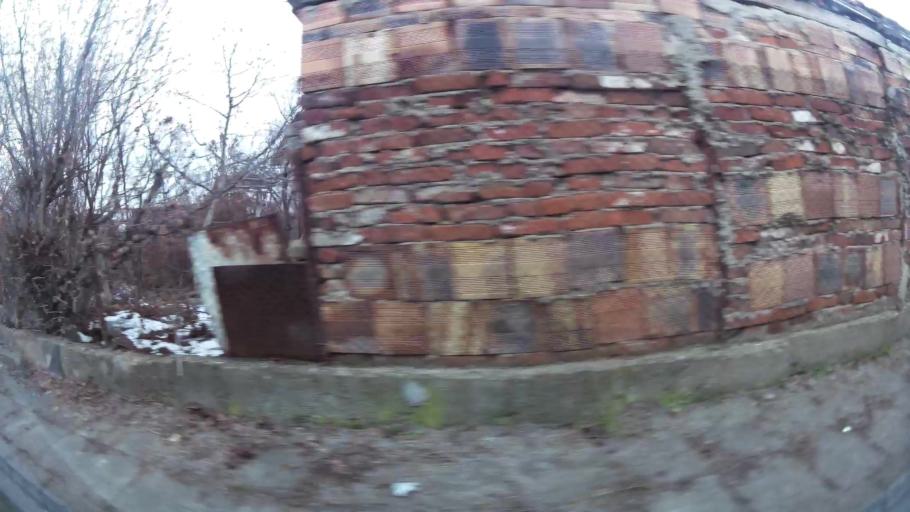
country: BG
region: Sofiya
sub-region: Obshtina Bozhurishte
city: Bozhurishte
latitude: 42.6976
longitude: 23.2182
